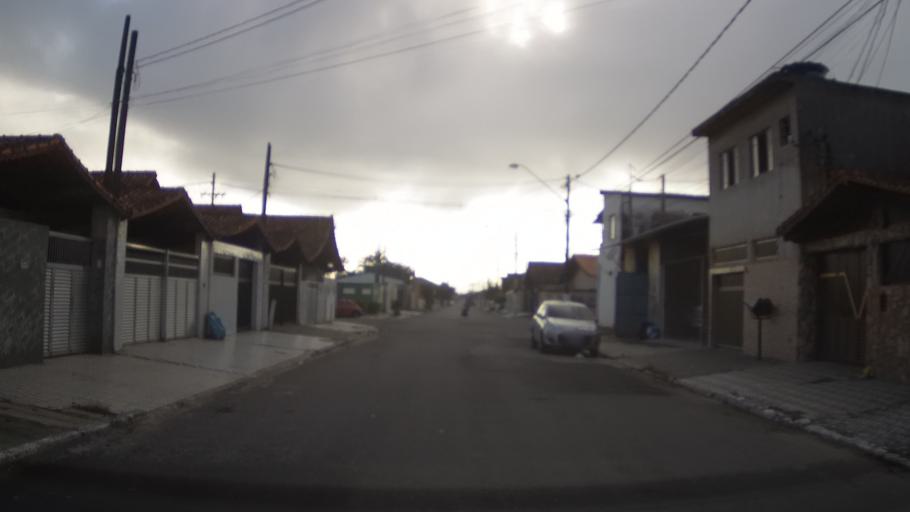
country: BR
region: Sao Paulo
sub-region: Praia Grande
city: Praia Grande
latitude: -24.0160
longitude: -46.4707
